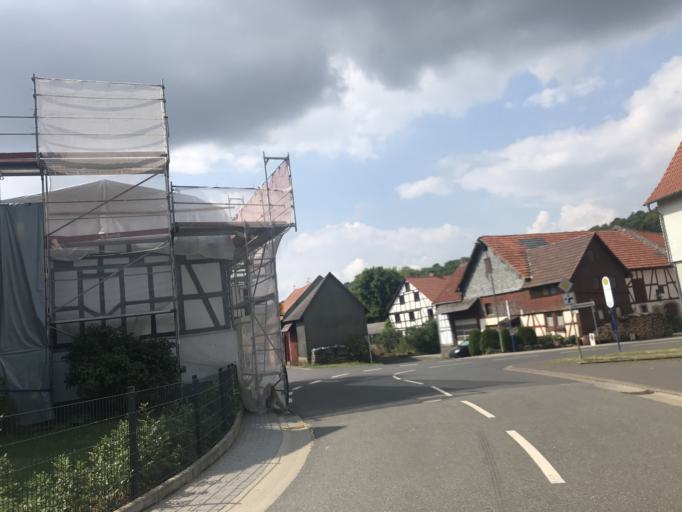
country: DE
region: Hesse
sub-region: Regierungsbezirk Giessen
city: Ulrichstein
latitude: 50.5741
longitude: 9.1244
